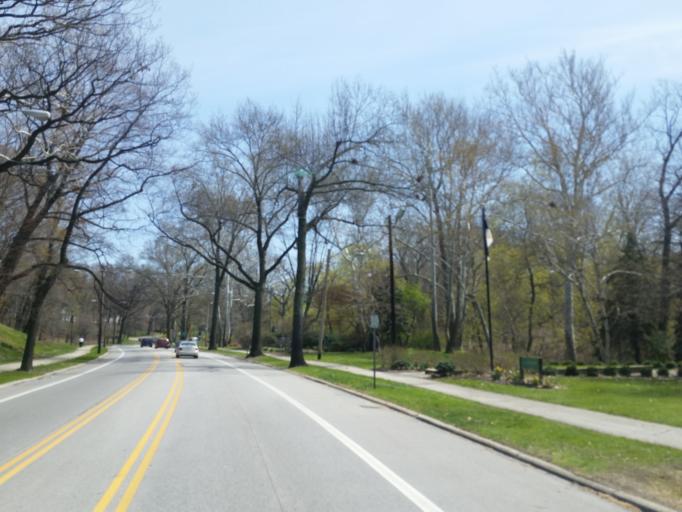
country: US
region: Ohio
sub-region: Cuyahoga County
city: Bratenahl
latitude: 41.5246
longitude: -81.6251
